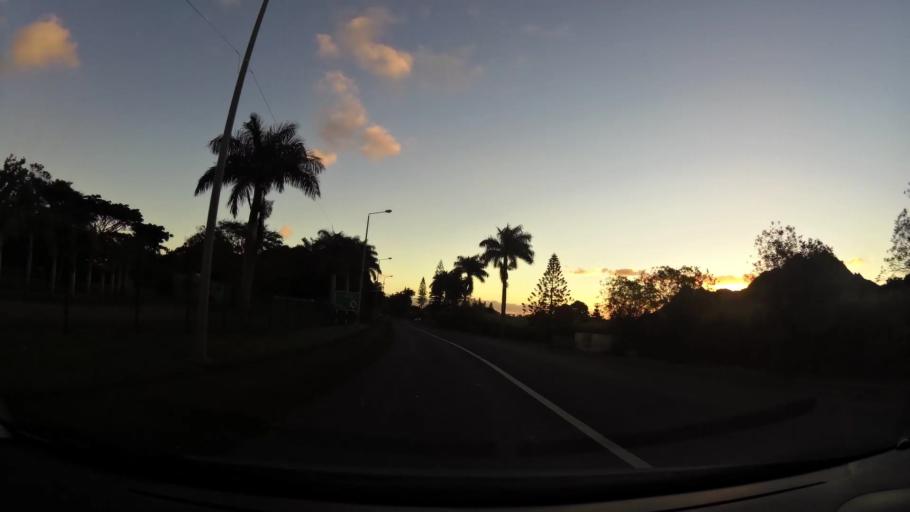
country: MU
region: Moka
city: Saint Pierre
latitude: -20.2231
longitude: 57.5320
